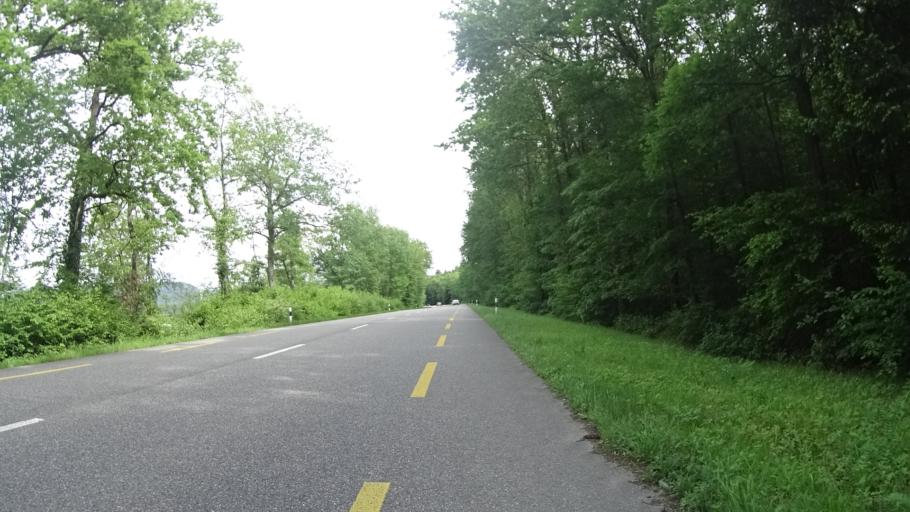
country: DE
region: Baden-Wuerttemberg
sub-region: Freiburg Region
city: Murg
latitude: 47.5522
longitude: 8.0094
